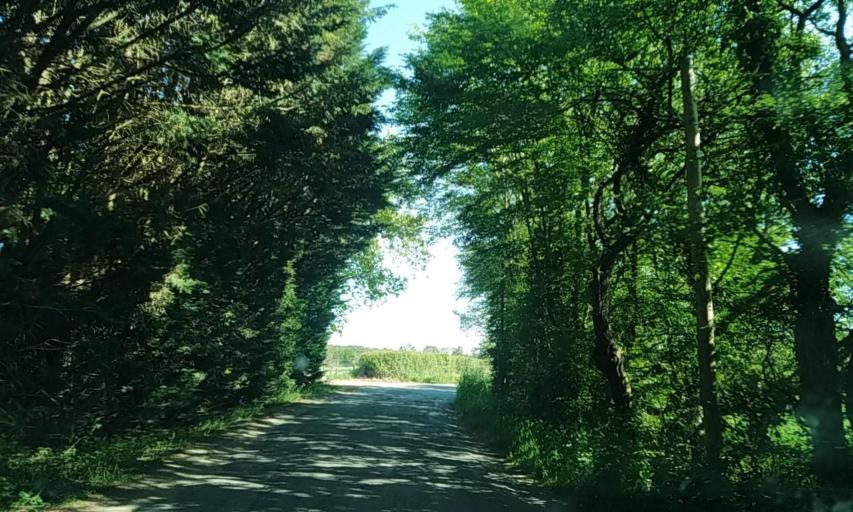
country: FR
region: Poitou-Charentes
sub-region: Departement des Deux-Sevres
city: Boisme
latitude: 46.8122
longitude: -0.4149
